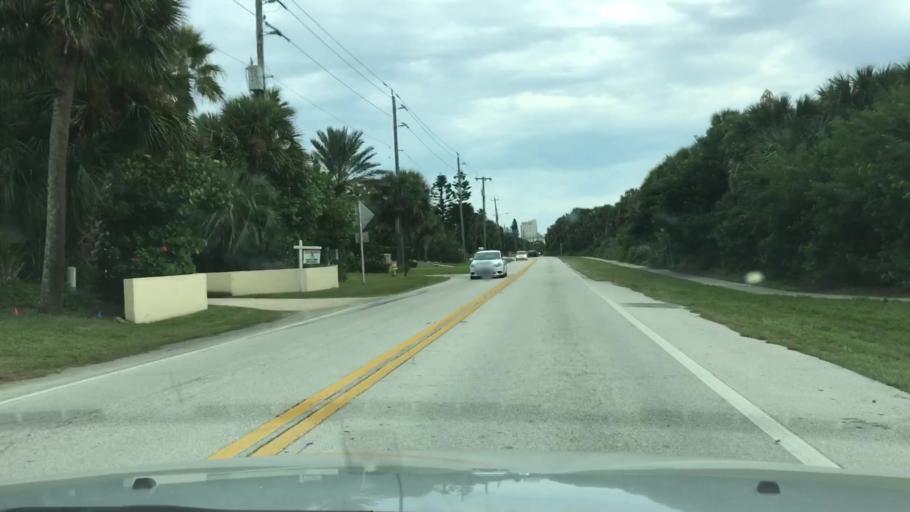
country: US
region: Florida
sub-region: Volusia County
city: Ormond Beach
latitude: 29.3003
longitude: -81.0441
